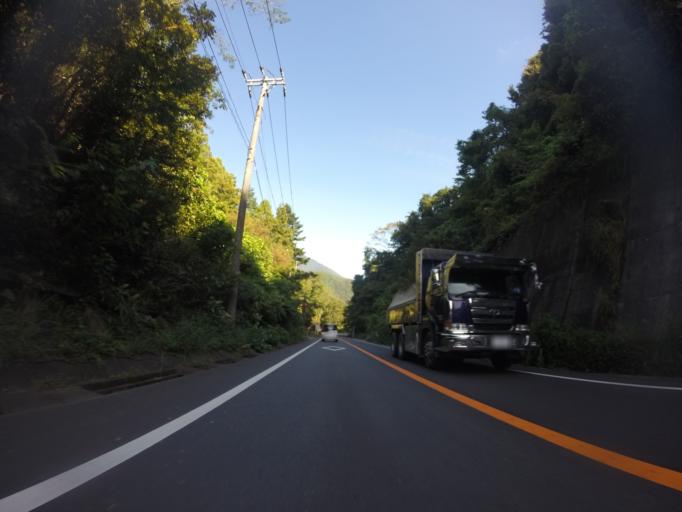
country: JP
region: Shizuoka
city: Fujinomiya
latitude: 35.3516
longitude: 138.4512
